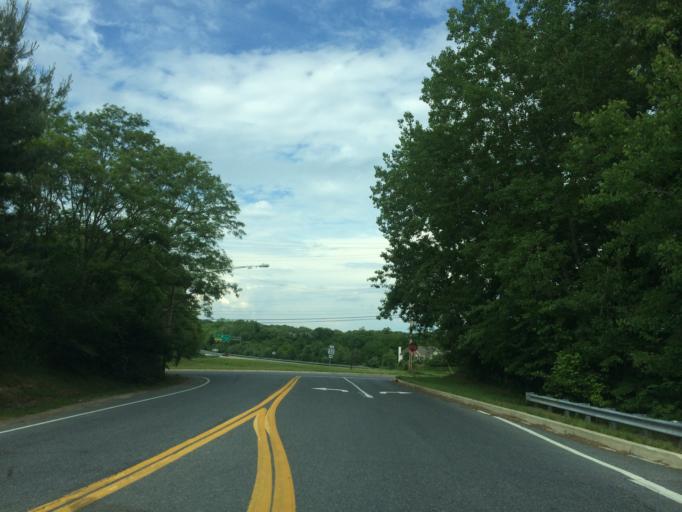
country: US
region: Maryland
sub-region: Howard County
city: Riverside
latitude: 39.1814
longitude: -76.9011
